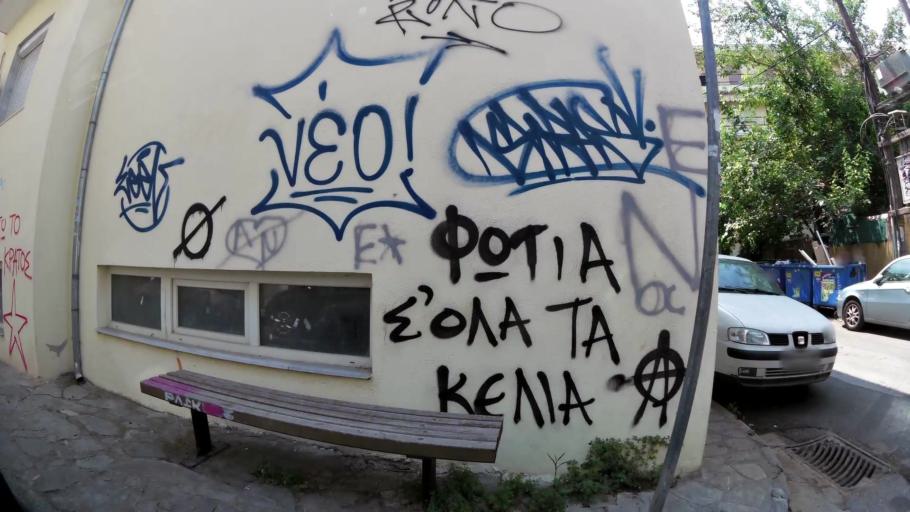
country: GR
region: Central Macedonia
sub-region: Nomos Thessalonikis
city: Agios Pavlos
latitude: 40.6350
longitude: 22.9605
